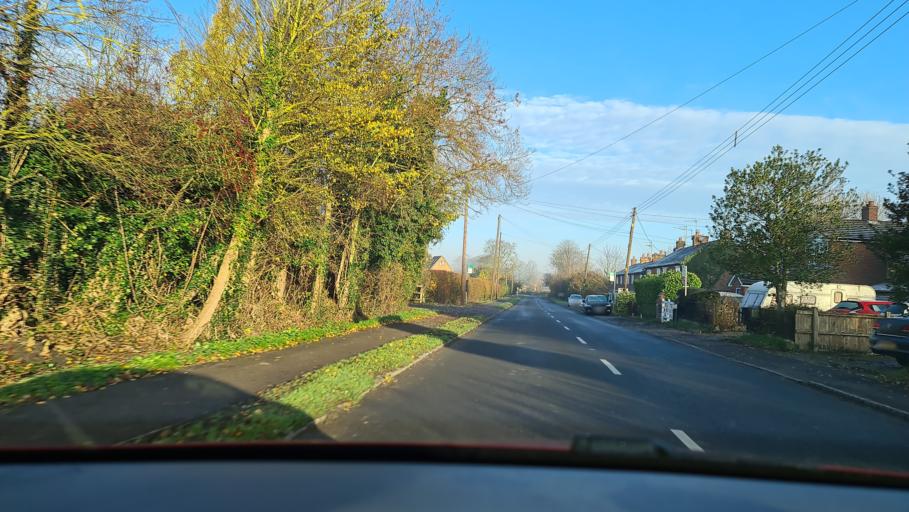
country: GB
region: England
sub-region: Buckinghamshire
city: Weston Turville
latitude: 51.7607
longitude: -0.7822
